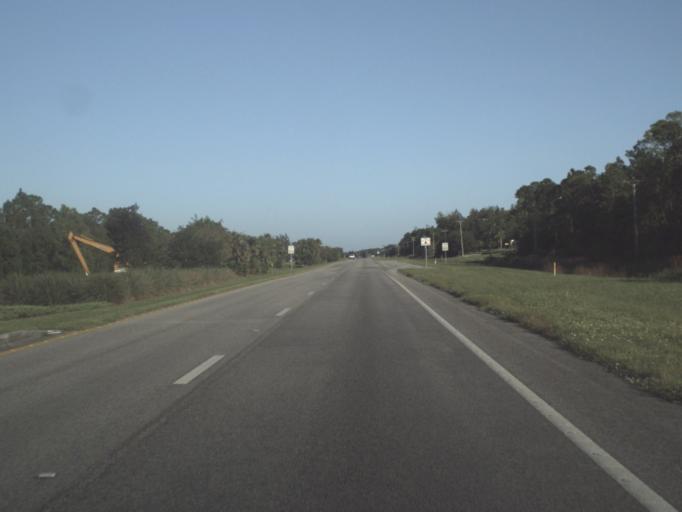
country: US
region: Florida
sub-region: Lee County
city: Suncoast Estates
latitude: 26.7555
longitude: -81.9231
